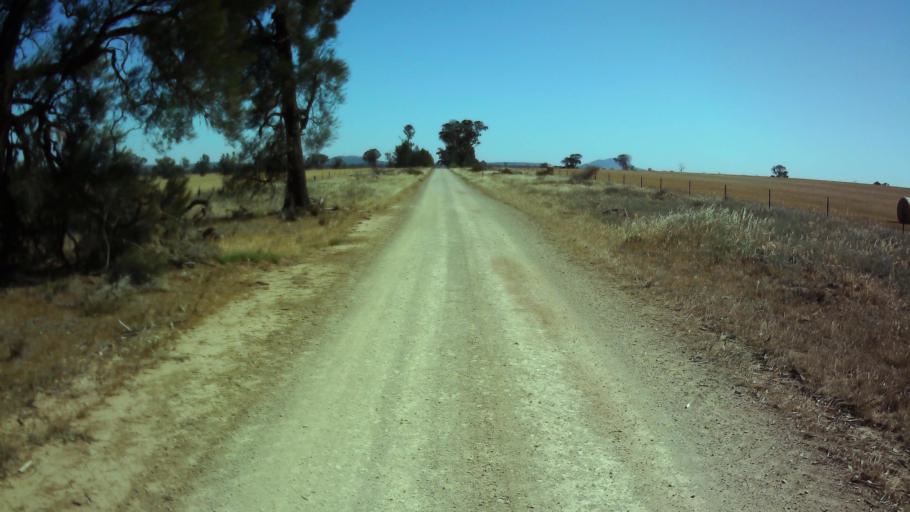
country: AU
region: New South Wales
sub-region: Weddin
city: Grenfell
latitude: -33.8781
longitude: 147.8737
